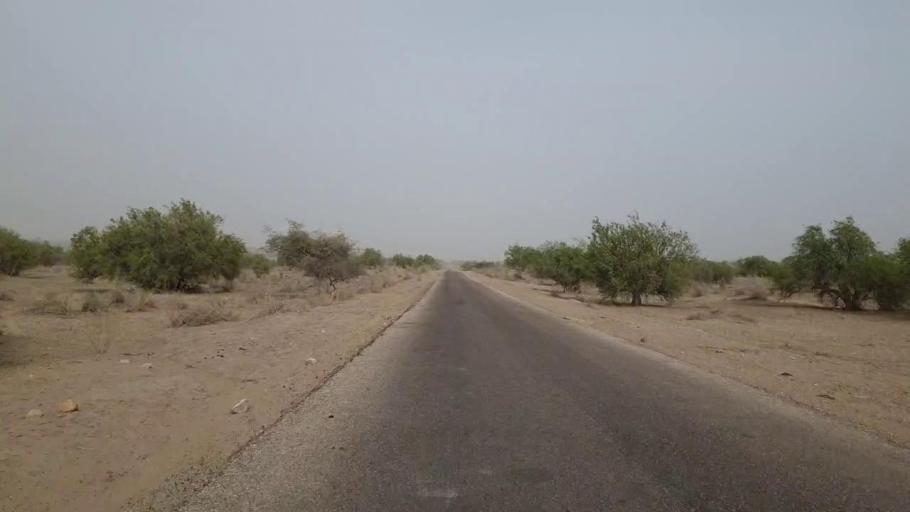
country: PK
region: Sindh
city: Islamkot
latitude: 24.5675
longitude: 70.3279
